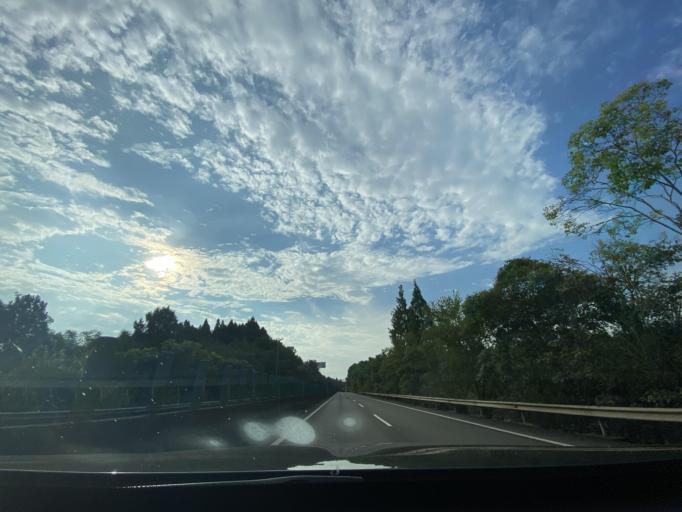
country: CN
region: Sichuan
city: Jiancheng
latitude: 30.2937
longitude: 104.5844
